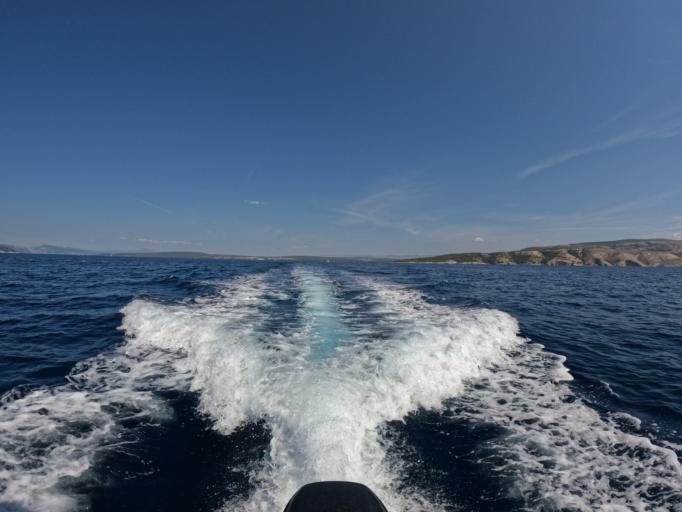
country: HR
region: Primorsko-Goranska
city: Punat
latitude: 44.9535
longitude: 14.6119
